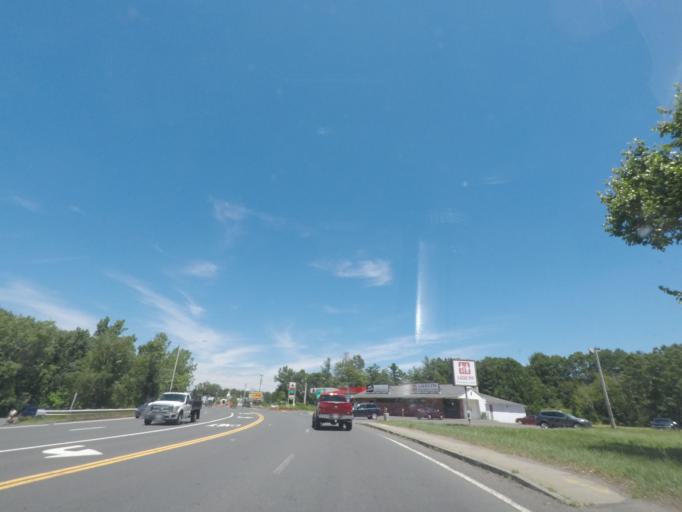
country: US
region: Massachusetts
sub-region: Hampden County
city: Westfield
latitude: 42.1397
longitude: -72.7347
